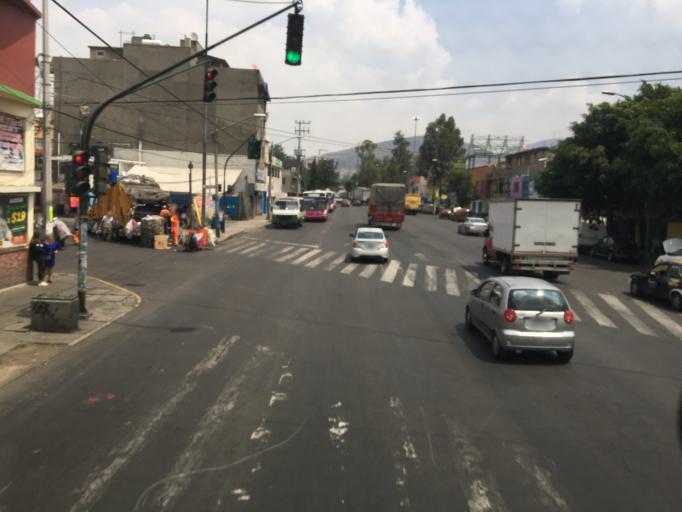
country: MX
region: Mexico
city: Colonia Lindavista
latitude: 19.5201
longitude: -99.1569
